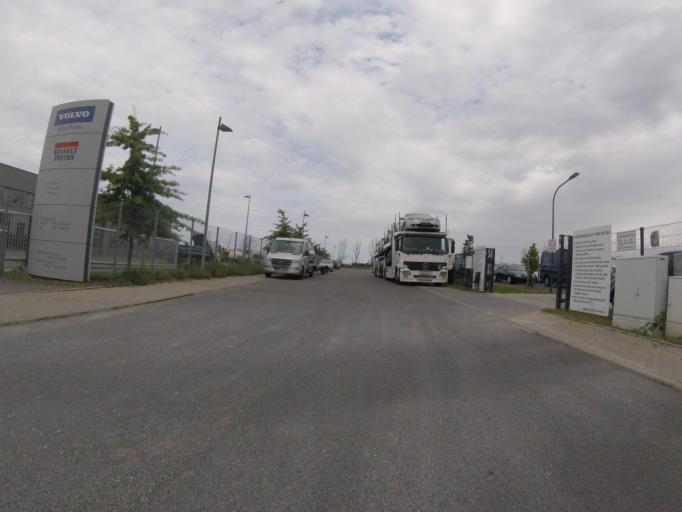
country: DE
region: Brandenburg
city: Wildau
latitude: 52.3207
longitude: 13.5989
